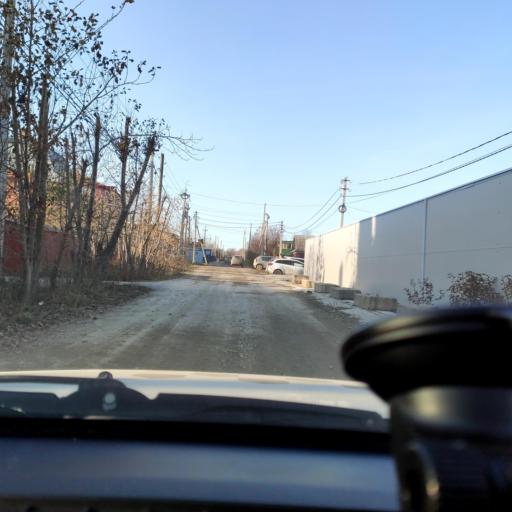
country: RU
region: Perm
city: Perm
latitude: 57.9891
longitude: 56.3069
